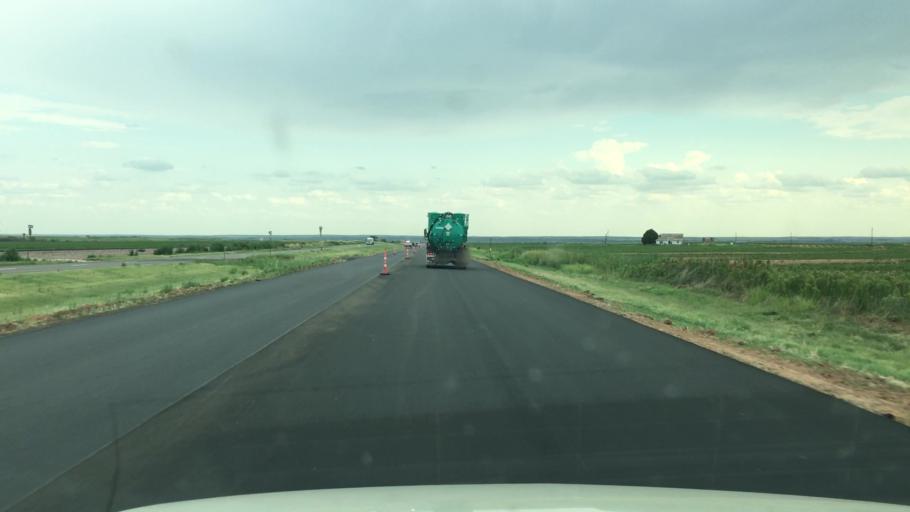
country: US
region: Texas
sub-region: Hall County
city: Memphis
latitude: 34.6186
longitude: -100.4716
